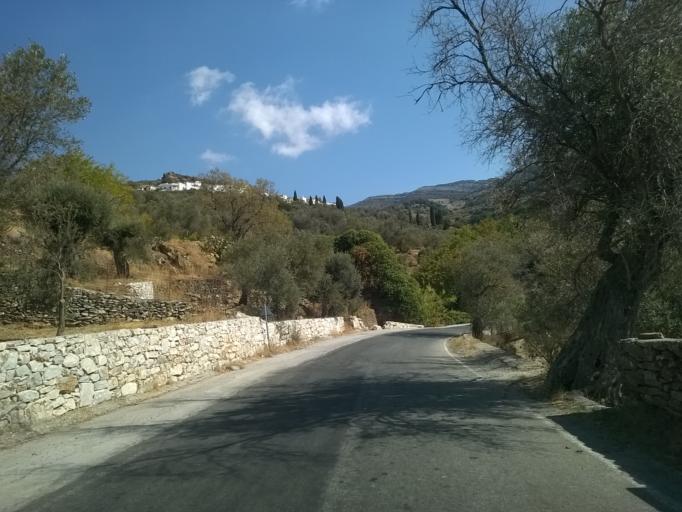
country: GR
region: South Aegean
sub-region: Nomos Kykladon
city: Filotion
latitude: 37.0789
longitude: 25.4934
